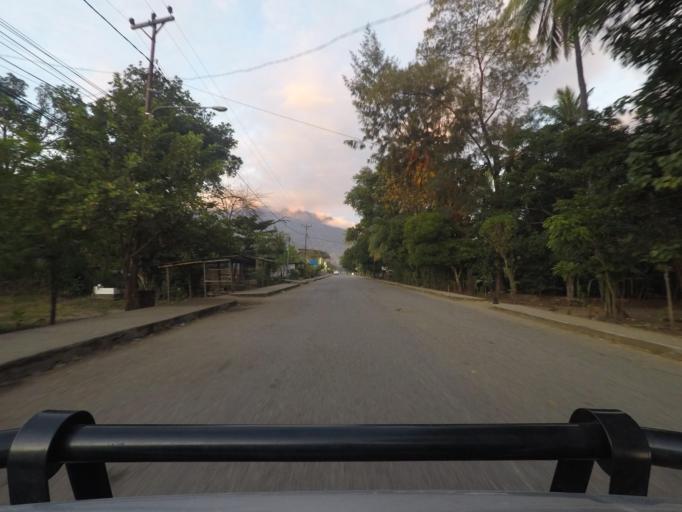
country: TL
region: Bobonaro
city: Maliana
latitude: -8.9899
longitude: 125.2068
